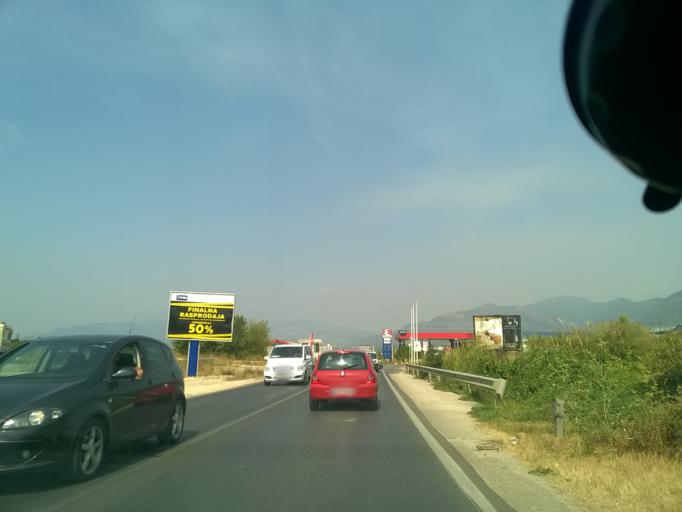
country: ME
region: Kotor
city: Kotor
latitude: 42.3795
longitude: 18.7493
